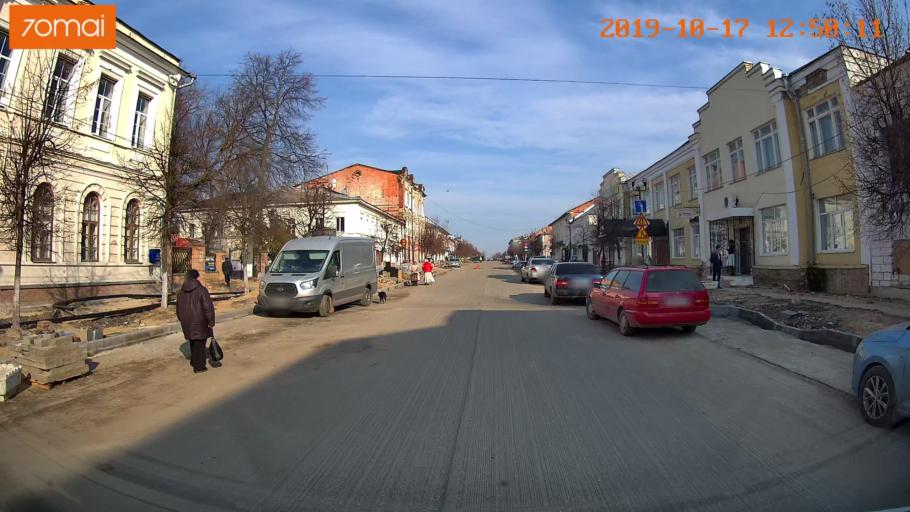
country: RU
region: Rjazan
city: Kasimov
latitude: 54.9374
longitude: 41.3917
